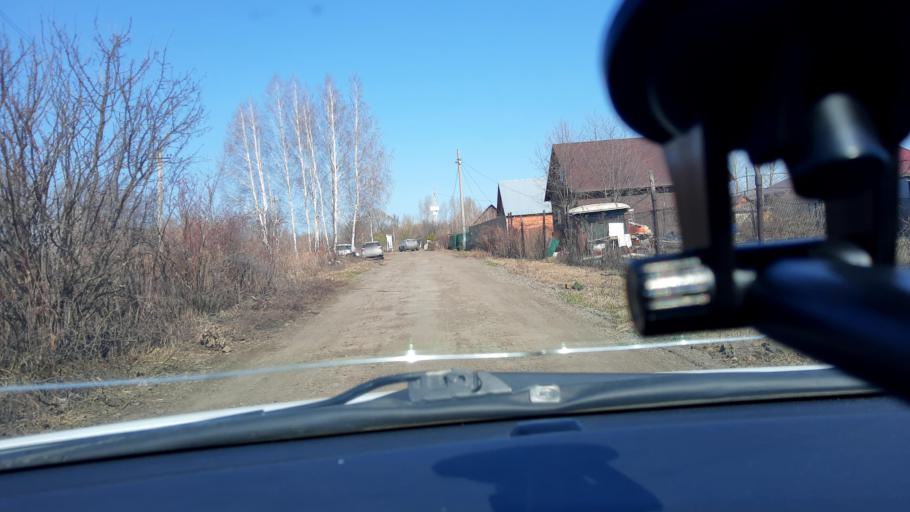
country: RU
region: Bashkortostan
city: Mikhaylovka
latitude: 54.7201
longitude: 55.8237
